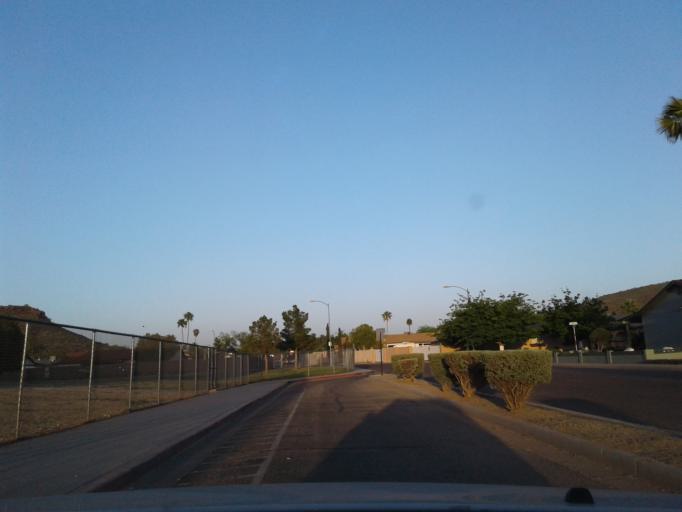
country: US
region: Arizona
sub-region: Maricopa County
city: Glendale
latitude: 33.6069
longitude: -112.0975
